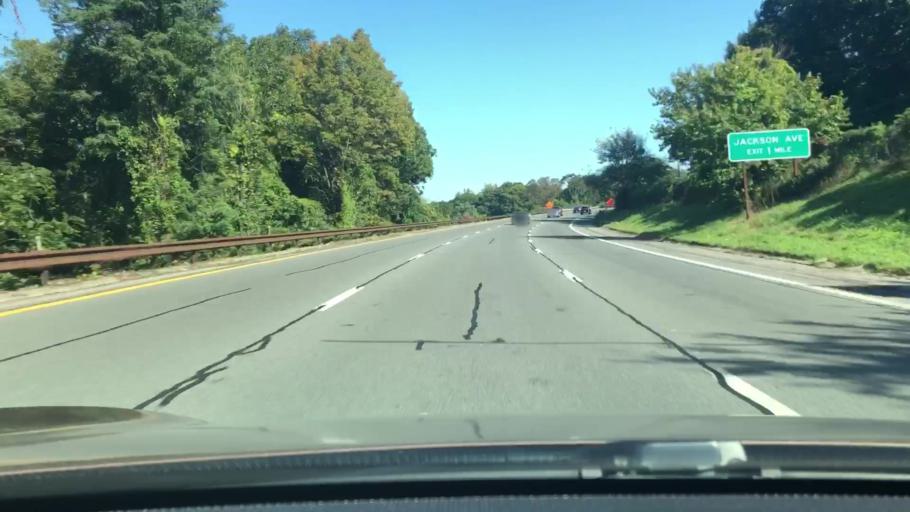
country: US
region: New York
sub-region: Westchester County
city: Tuckahoe
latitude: 40.9699
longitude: -73.8493
